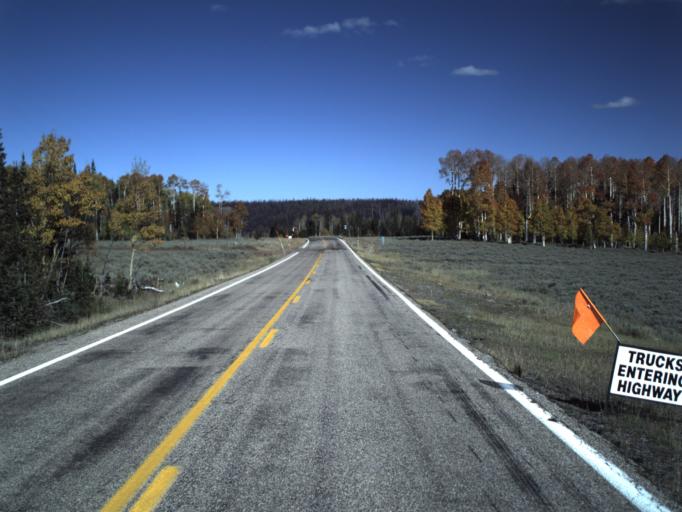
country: US
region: Utah
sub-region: Iron County
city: Parowan
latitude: 37.6586
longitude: -112.7466
